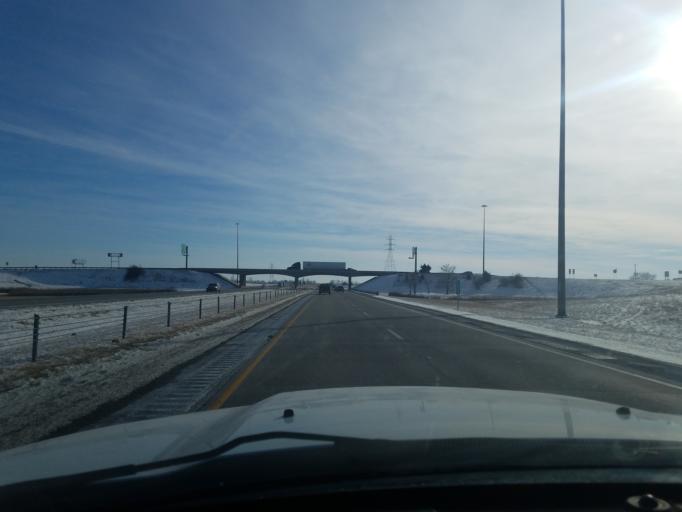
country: US
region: Indiana
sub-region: Grant County
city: Upland
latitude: 40.4247
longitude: -85.5497
